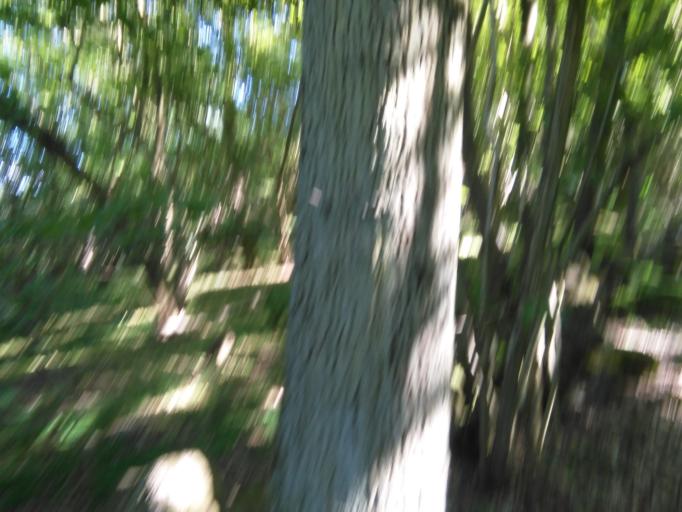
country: DK
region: Capital Region
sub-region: Bornholm Kommune
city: Ronne
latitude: 55.2567
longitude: 14.7706
